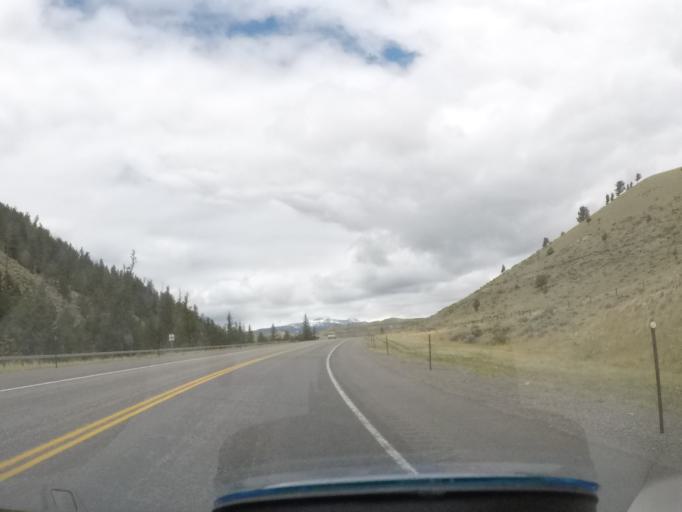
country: US
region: Wyoming
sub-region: Sublette County
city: Pinedale
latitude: 43.5795
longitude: -109.7619
